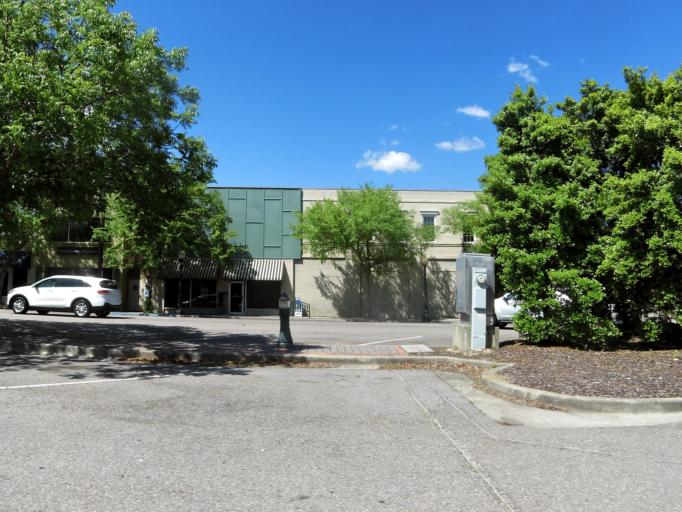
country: US
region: South Carolina
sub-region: Aiken County
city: Aiken
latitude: 33.5618
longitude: -81.7230
